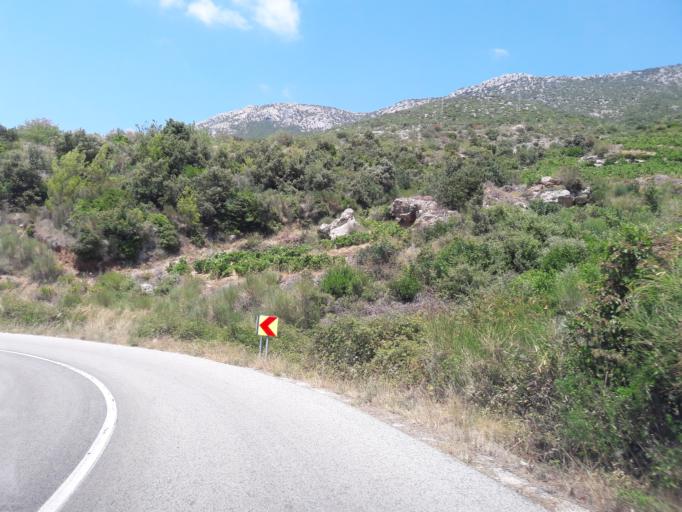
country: HR
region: Dubrovacko-Neretvanska
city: Orebic
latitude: 42.9736
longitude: 17.2413
